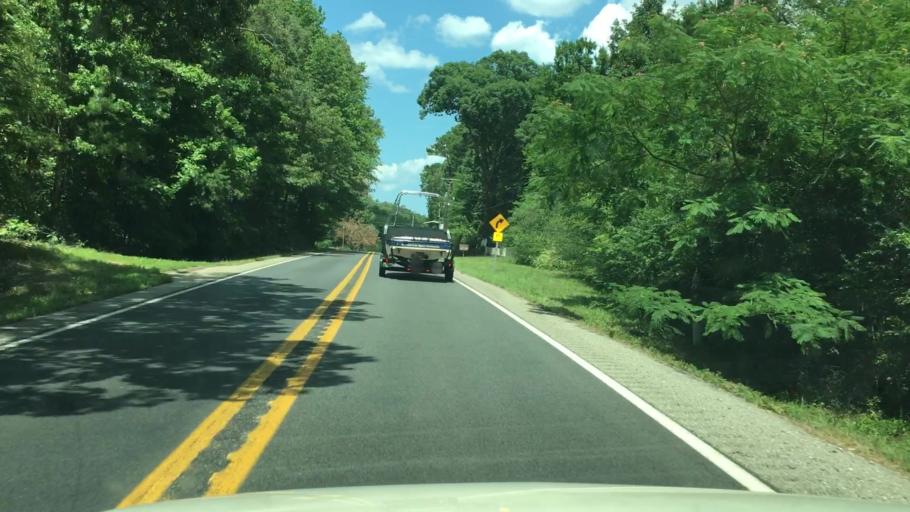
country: US
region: Arkansas
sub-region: Garland County
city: Lake Hamilton
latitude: 34.3872
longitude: -93.1221
